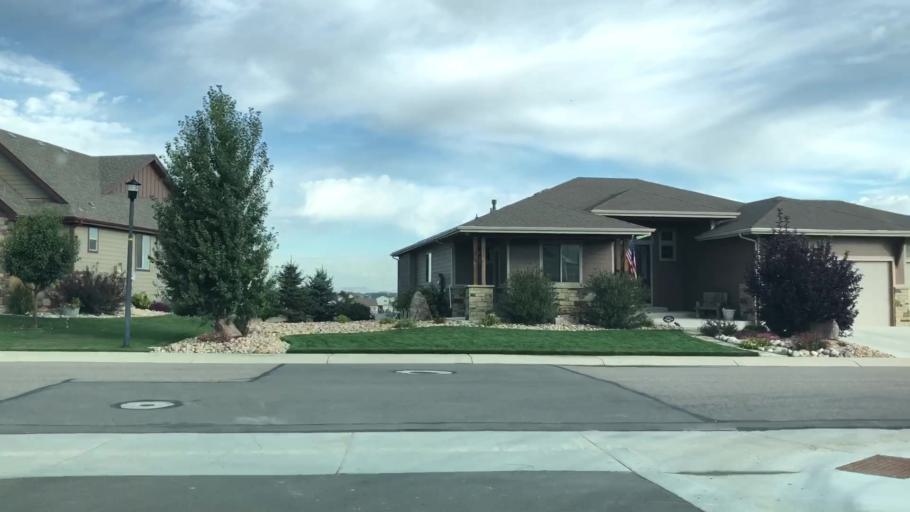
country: US
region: Colorado
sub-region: Weld County
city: Windsor
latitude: 40.4439
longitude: -104.9681
